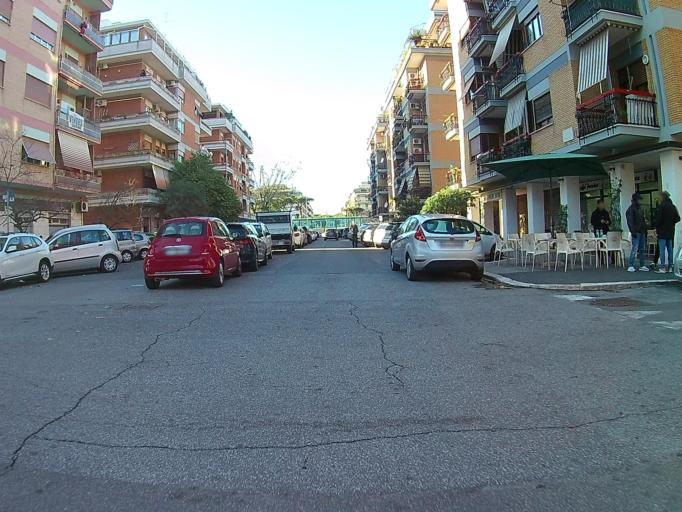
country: IT
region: Latium
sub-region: Citta metropolitana di Roma Capitale
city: Lido di Ostia
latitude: 41.7383
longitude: 12.2850
